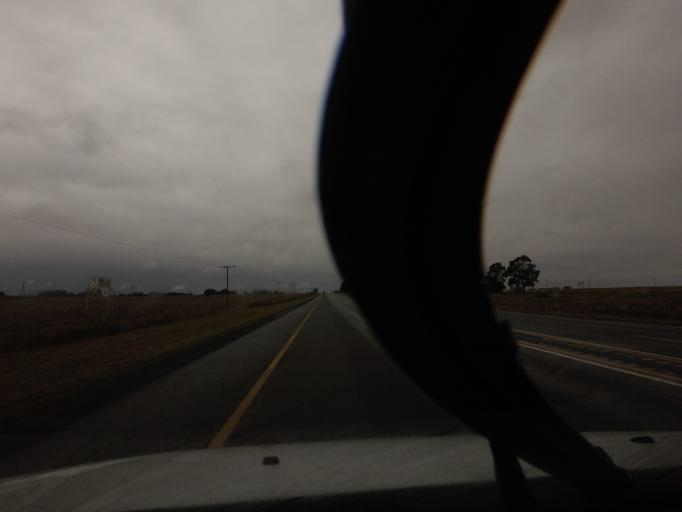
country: ZA
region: Mpumalanga
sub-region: Nkangala District Municipality
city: Belfast
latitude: -25.7231
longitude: 30.0396
